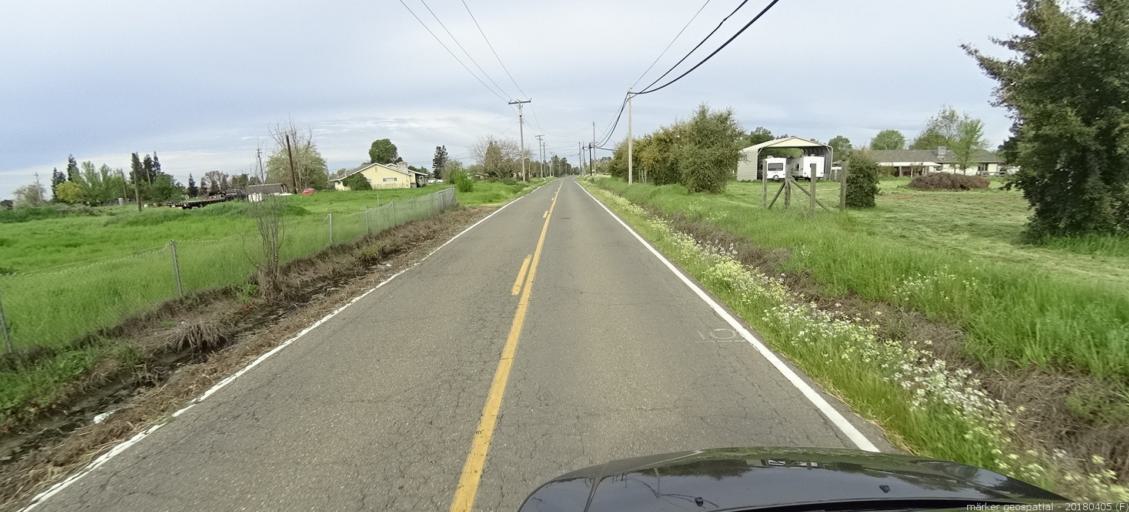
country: US
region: California
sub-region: Sacramento County
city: Herald
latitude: 38.2917
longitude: -121.2427
